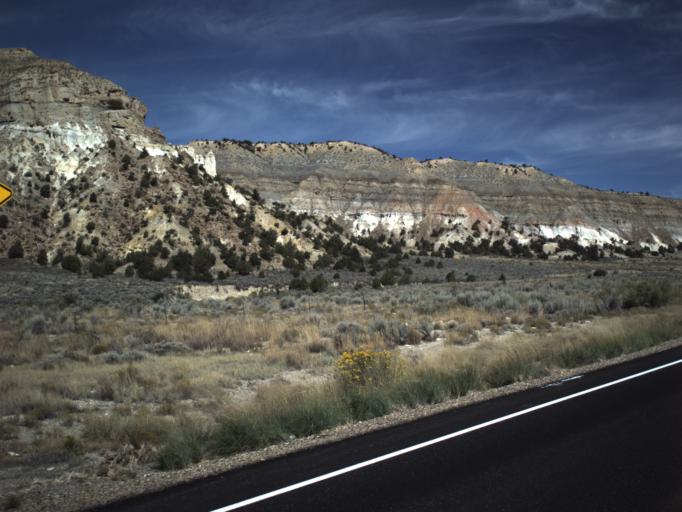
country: US
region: Utah
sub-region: Garfield County
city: Panguitch
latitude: 37.5853
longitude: -111.9836
